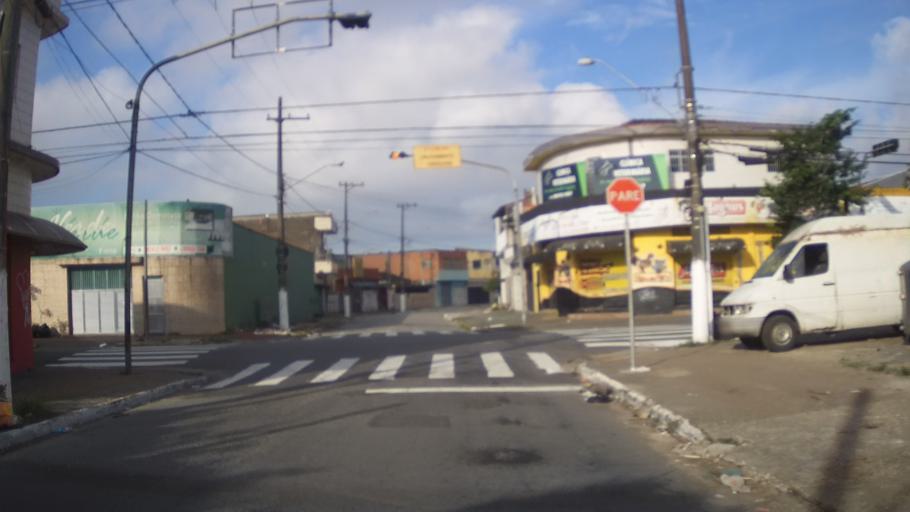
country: BR
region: Sao Paulo
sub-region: Praia Grande
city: Praia Grande
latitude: -24.0184
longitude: -46.4762
